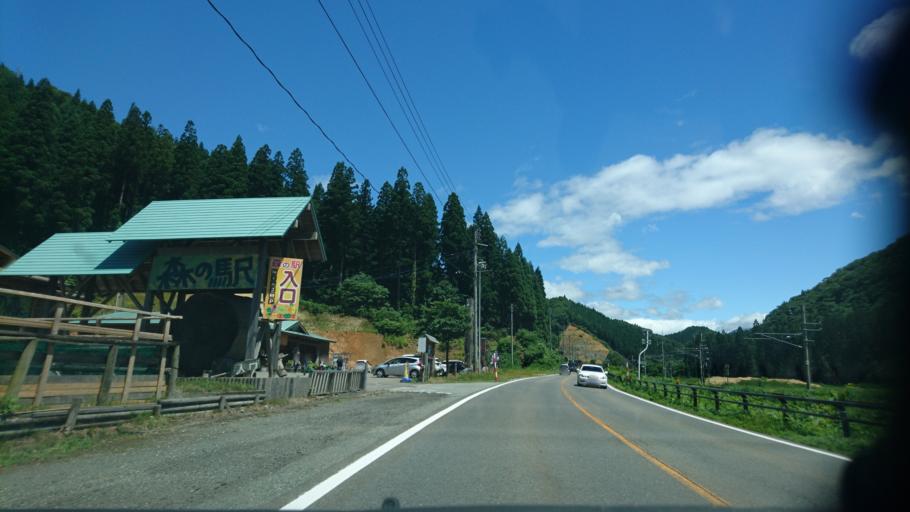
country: JP
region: Akita
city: Kakunodatemachi
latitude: 39.6474
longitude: 140.6649
